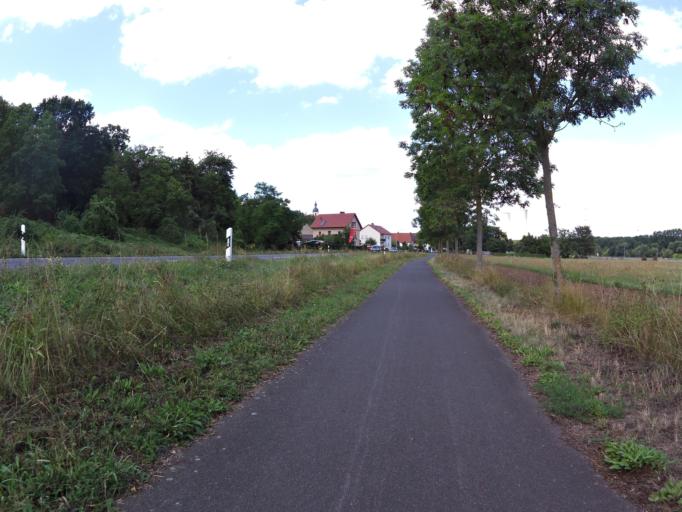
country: DE
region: Bavaria
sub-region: Regierungsbezirk Unterfranken
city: Grafenrheinfeld
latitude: 49.9700
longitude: 10.1724
